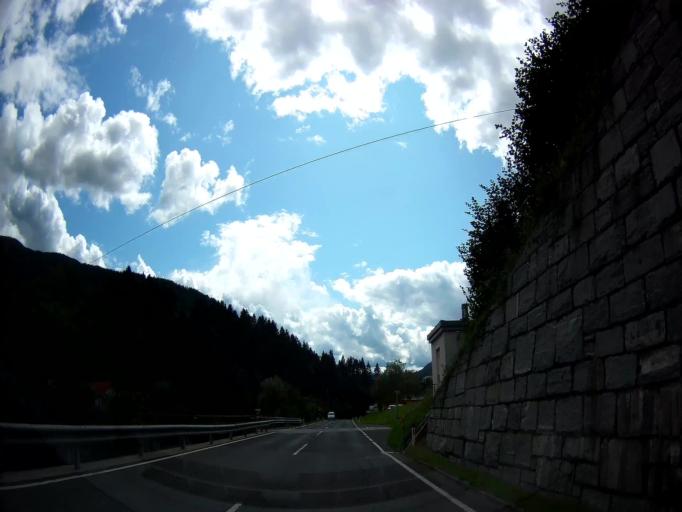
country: AT
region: Carinthia
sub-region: Politischer Bezirk Spittal an der Drau
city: Gmuend
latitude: 46.8939
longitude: 13.5254
